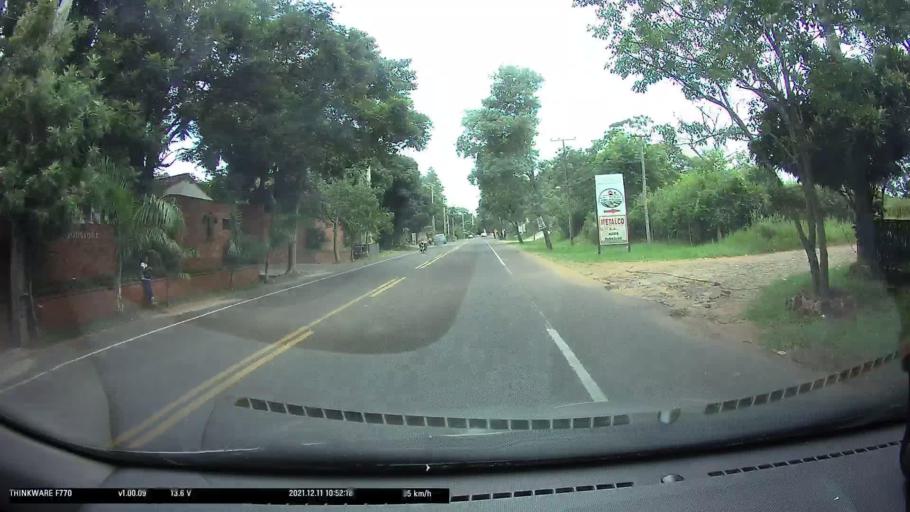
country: PY
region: Cordillera
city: San Bernardino
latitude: -25.2932
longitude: -57.2688
